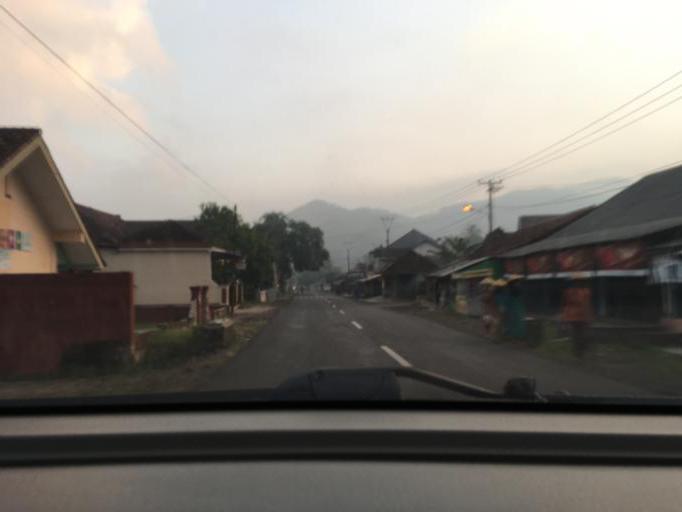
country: ID
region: West Java
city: Kampungdesa Pamokolan
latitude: -7.1995
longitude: 108.1996
